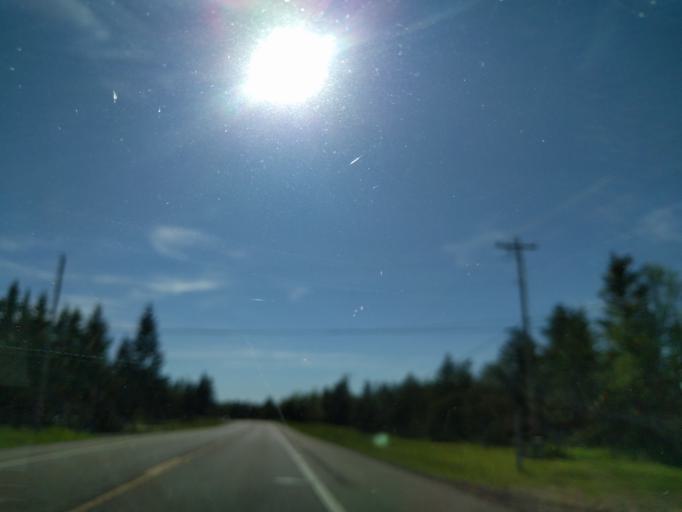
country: US
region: Michigan
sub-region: Marquette County
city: K. I. Sawyer Air Force Base
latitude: 46.2837
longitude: -87.3763
